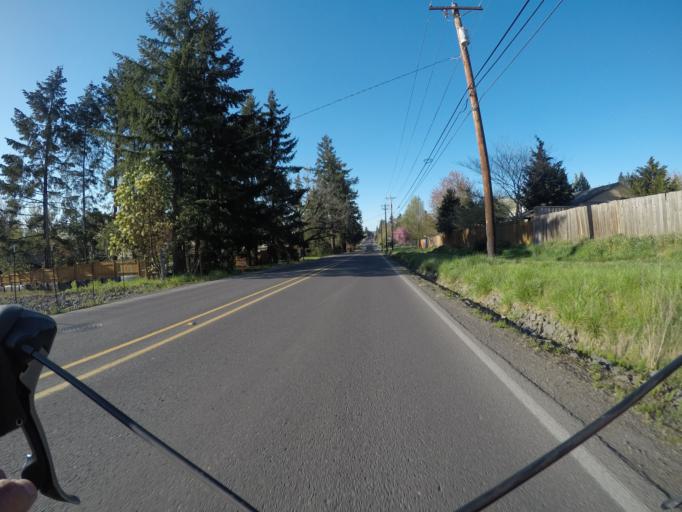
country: US
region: Oregon
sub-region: Washington County
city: Aloha
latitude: 45.4708
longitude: -122.8675
